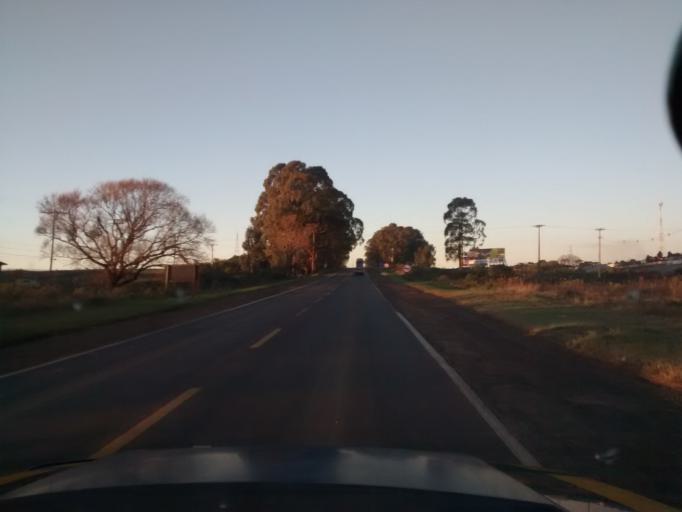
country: BR
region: Rio Grande do Sul
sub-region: Vacaria
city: Vacaria
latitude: -28.4969
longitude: -50.9157
